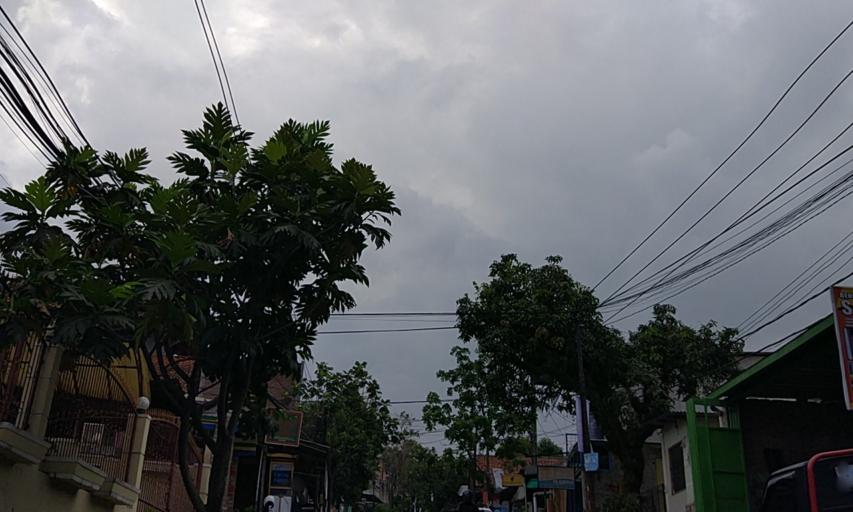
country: ID
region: West Java
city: Bandung
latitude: -6.9010
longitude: 107.6806
